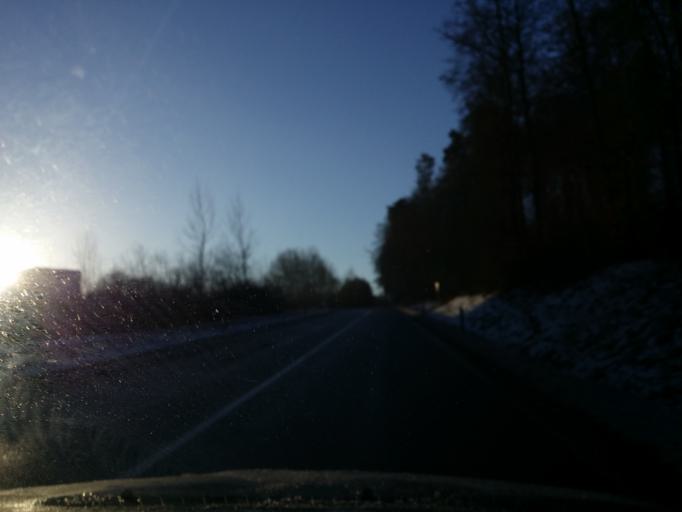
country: DE
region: Hesse
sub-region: Regierungsbezirk Darmstadt
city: Niedernhausen
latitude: 50.1496
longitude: 8.3268
